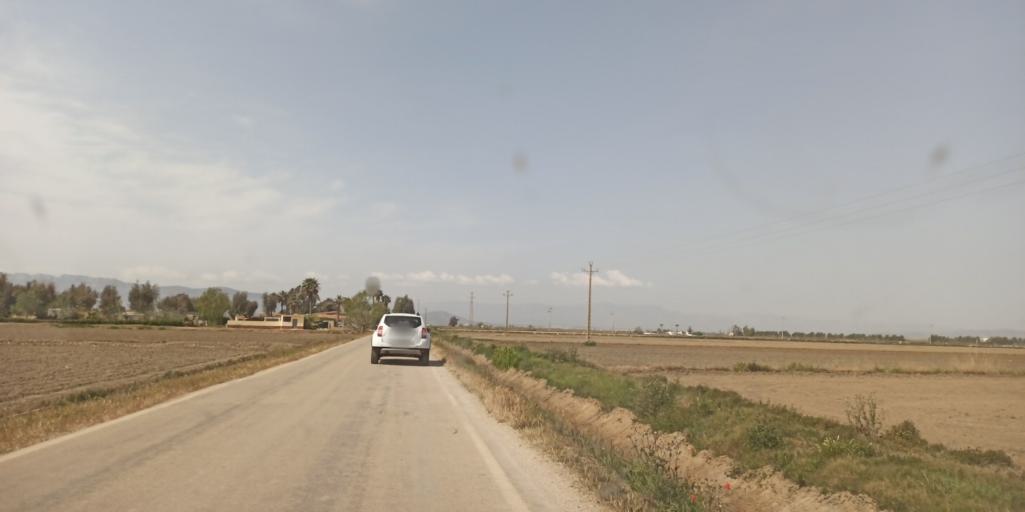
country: ES
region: Catalonia
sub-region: Provincia de Tarragona
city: Deltebre
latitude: 40.6455
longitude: 0.7205
